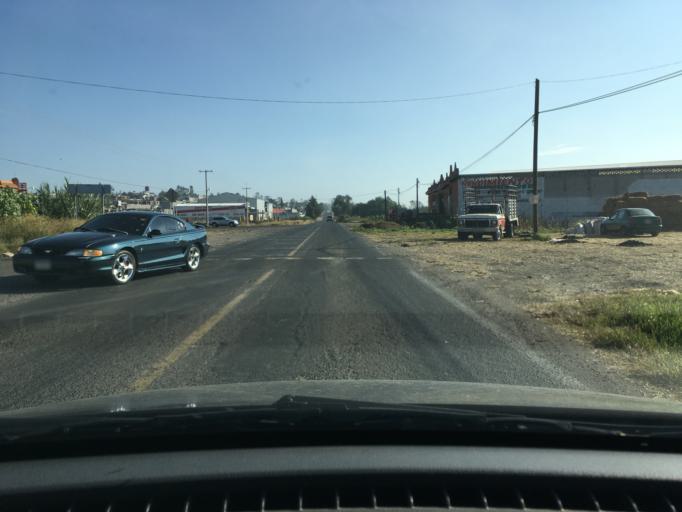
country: MX
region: Michoacan
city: Alvaro Obregon
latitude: 19.8095
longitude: -101.0588
